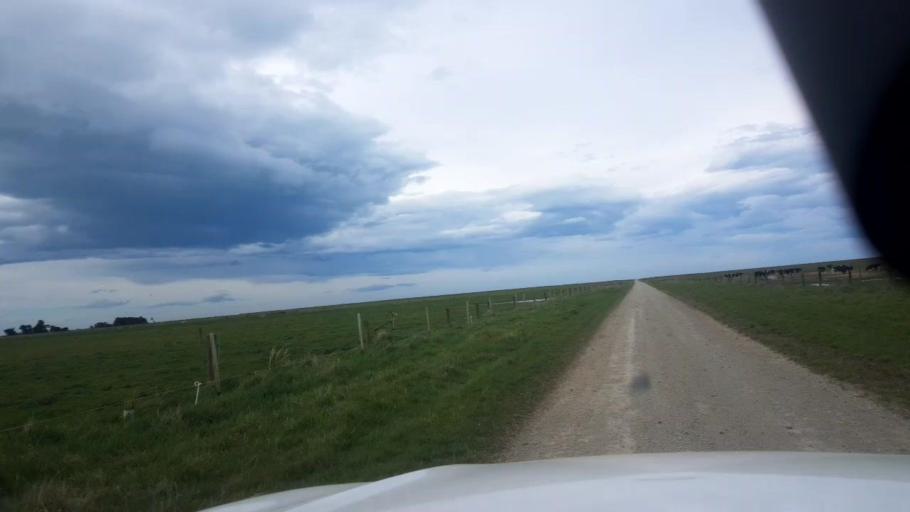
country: NZ
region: Canterbury
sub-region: Timaru District
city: Timaru
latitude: -44.3047
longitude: 171.3067
